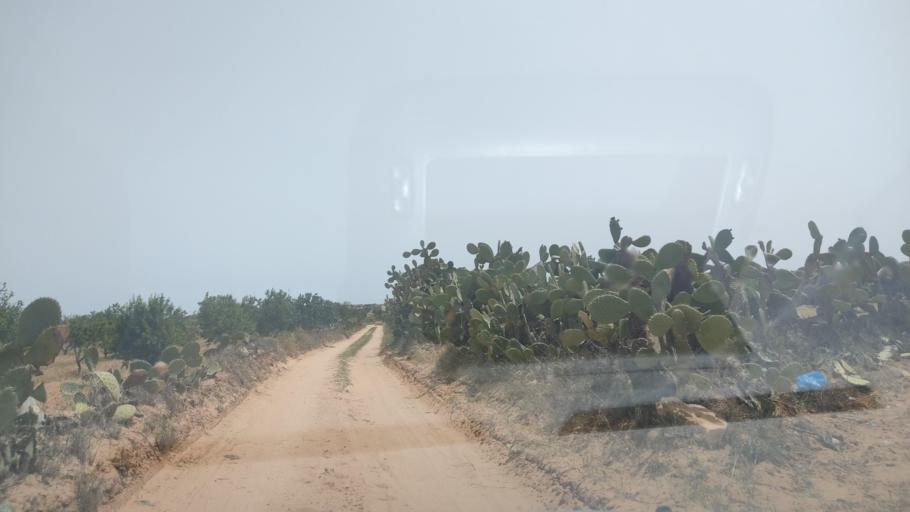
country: TN
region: Safaqis
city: Sfax
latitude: 34.8343
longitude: 10.5998
